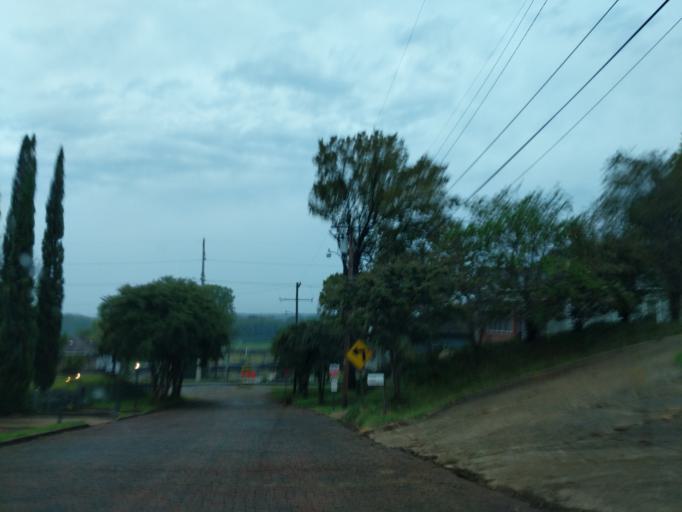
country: US
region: Mississippi
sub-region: Warren County
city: Vicksburg
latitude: 32.3415
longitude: -90.8861
